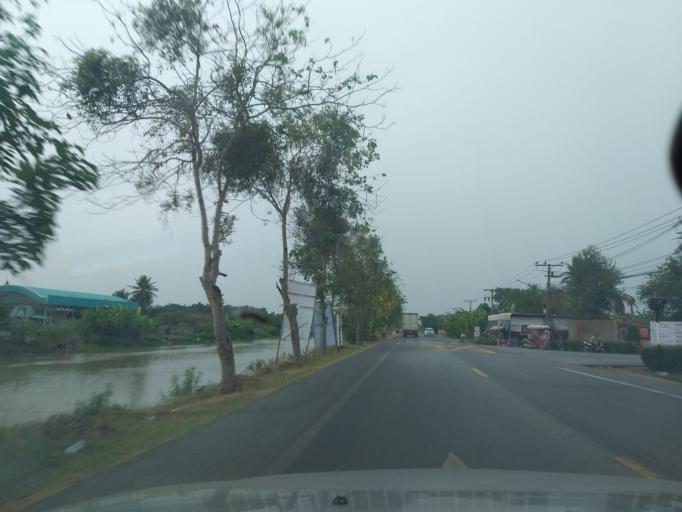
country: TH
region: Pathum Thani
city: Ban Lam Luk Ka
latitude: 13.9951
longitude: 100.8951
